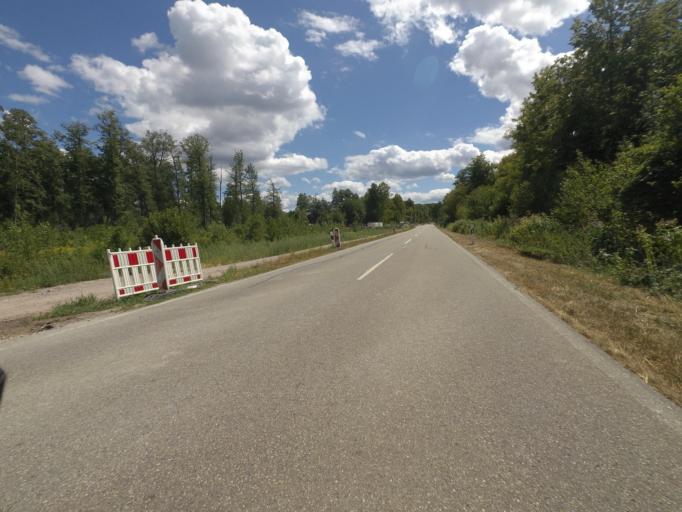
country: DE
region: Baden-Wuerttemberg
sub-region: Karlsruhe Region
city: Ottenhofen
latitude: 48.7449
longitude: 8.1067
